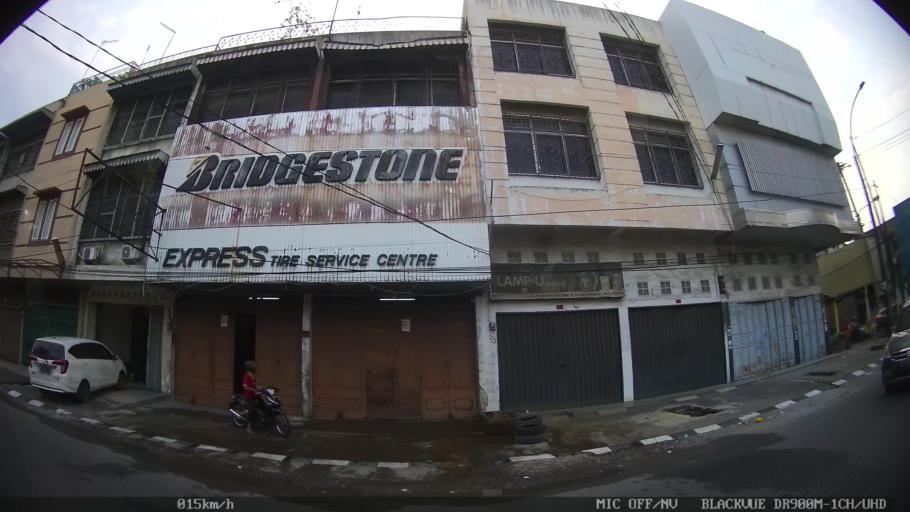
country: ID
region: North Sumatra
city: Medan
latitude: 3.5955
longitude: 98.6882
